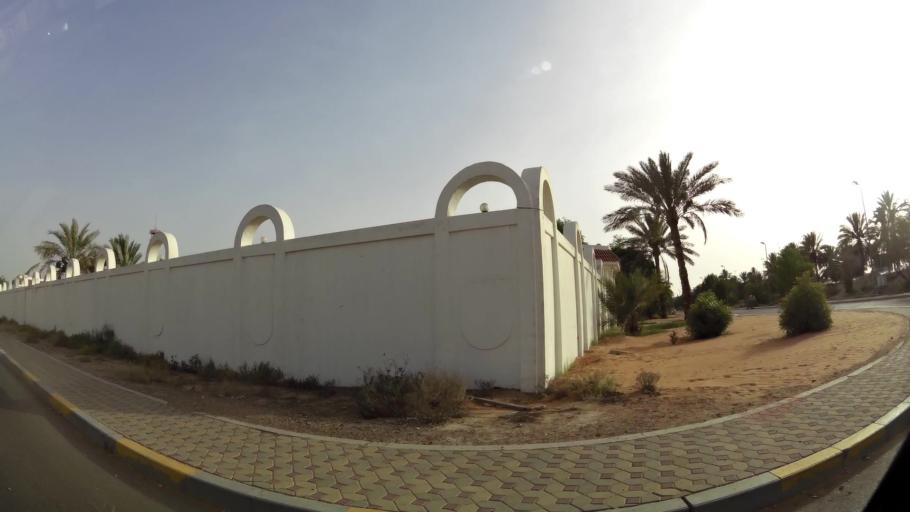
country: AE
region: Abu Dhabi
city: Al Ain
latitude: 24.2295
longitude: 55.7183
